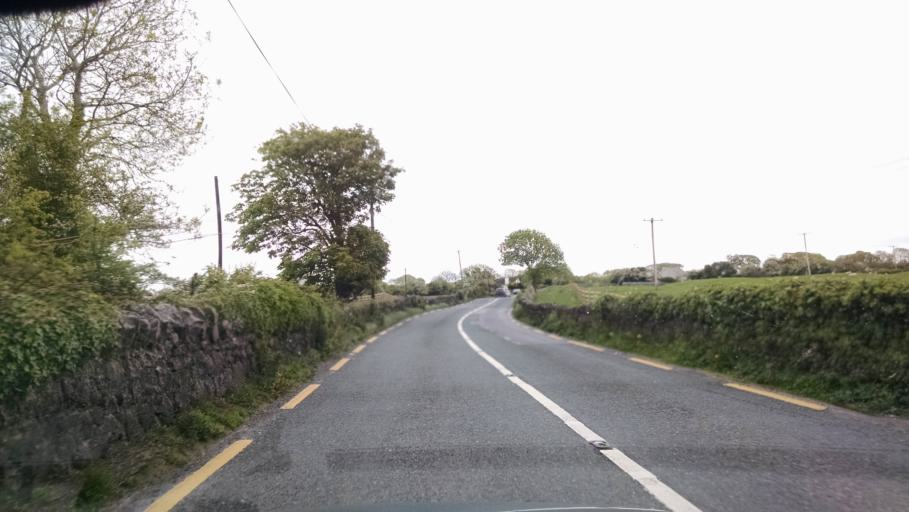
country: IE
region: Connaught
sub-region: County Galway
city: Moycullen
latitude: 53.4379
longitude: -9.0655
